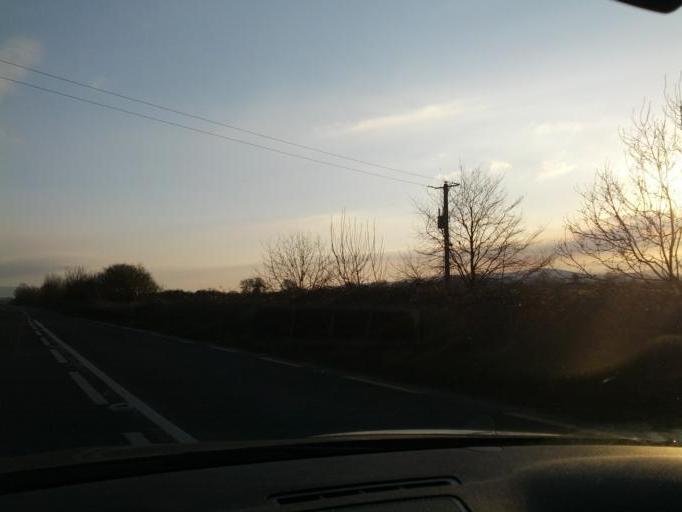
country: IE
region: Munster
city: Nenagh Bridge
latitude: 52.8912
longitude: -8.1890
